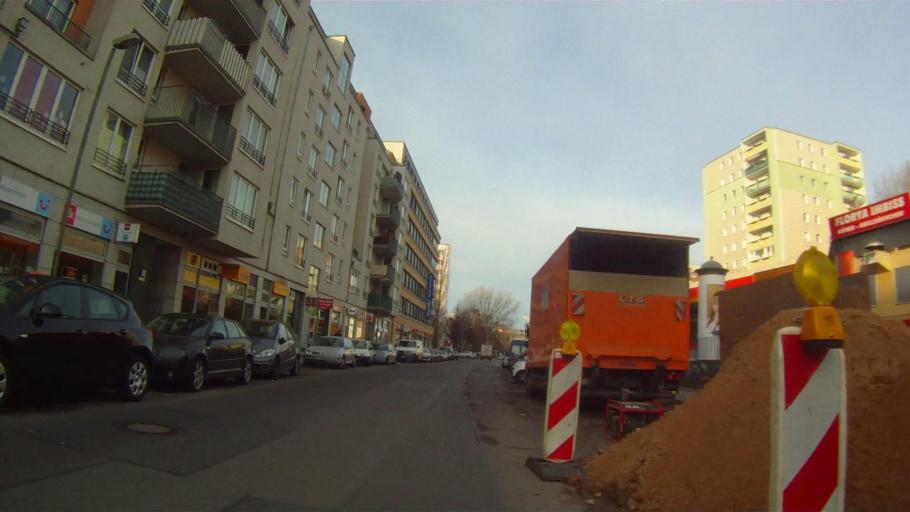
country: DE
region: Berlin
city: Bezirk Kreuzberg
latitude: 52.5074
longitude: 13.4155
